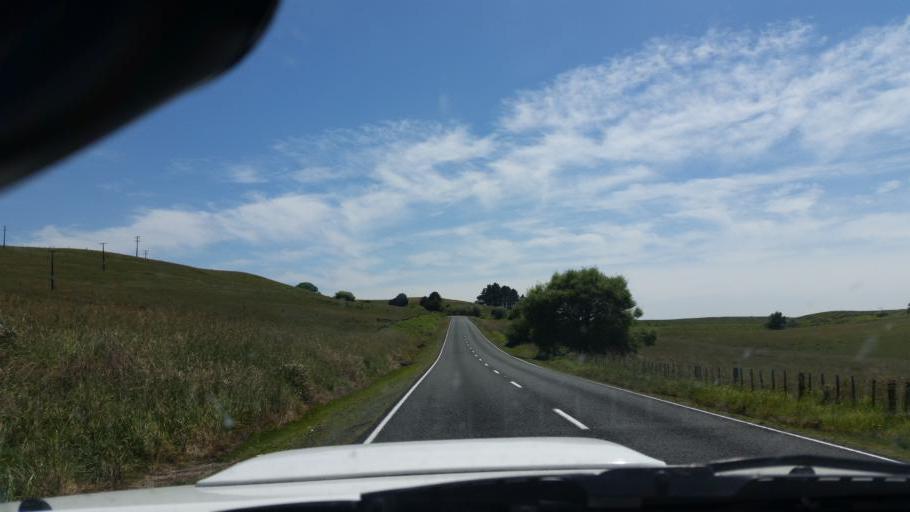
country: NZ
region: Auckland
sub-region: Auckland
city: Wellsford
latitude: -36.1877
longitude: 174.4092
